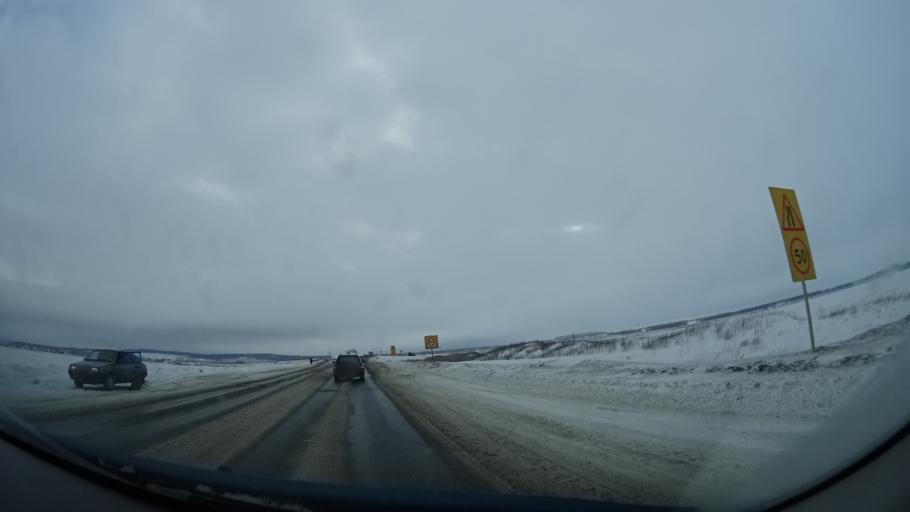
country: RU
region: Bashkortostan
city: Mikhaylovka
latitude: 54.8837
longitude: 55.7159
